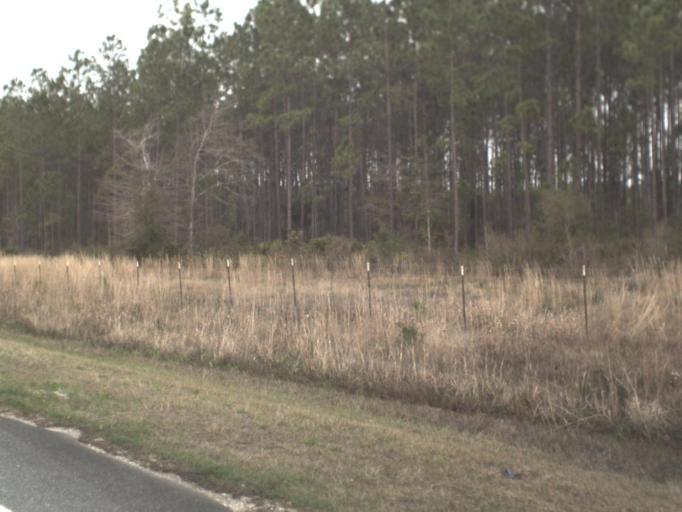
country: US
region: Florida
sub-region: Leon County
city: Woodville
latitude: 30.1991
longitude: -84.1658
